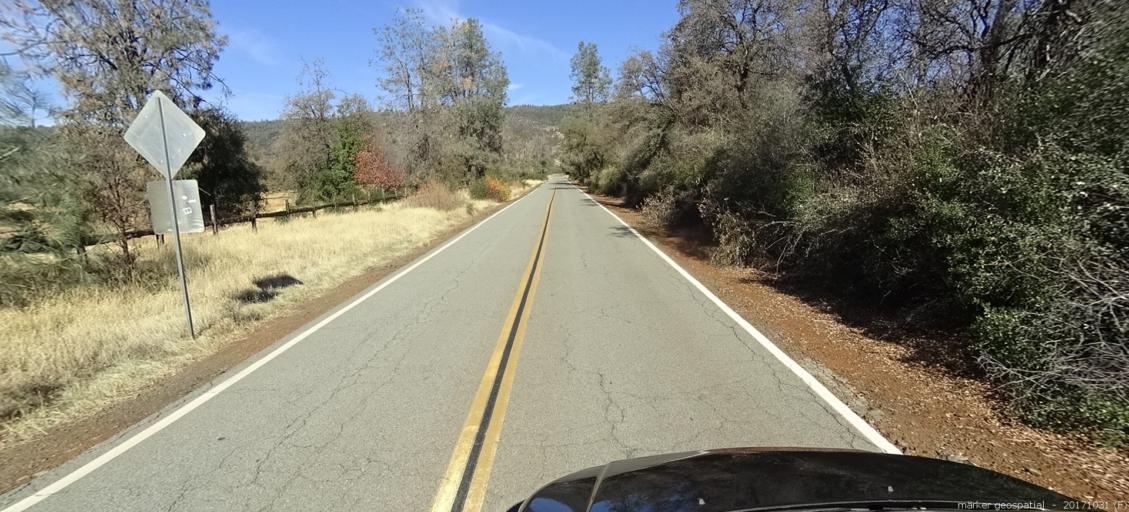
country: US
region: California
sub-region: Shasta County
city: Shingletown
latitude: 40.4469
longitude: -121.8994
